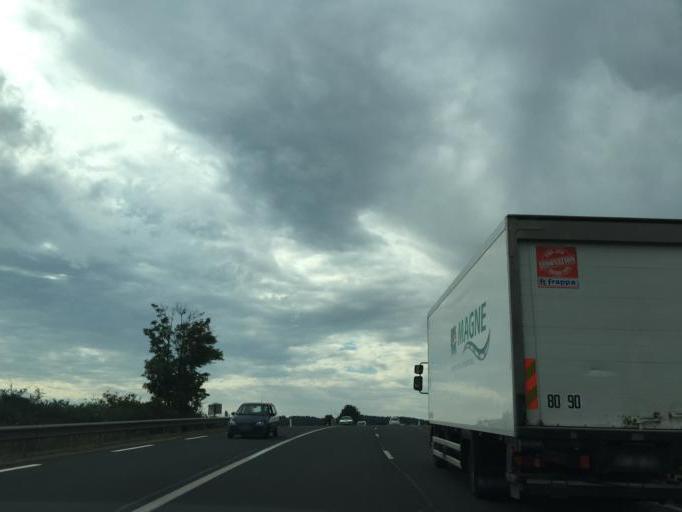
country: FR
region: Auvergne
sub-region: Departement de la Haute-Loire
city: Solignac-sur-Loire
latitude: 44.9136
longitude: 3.8478
